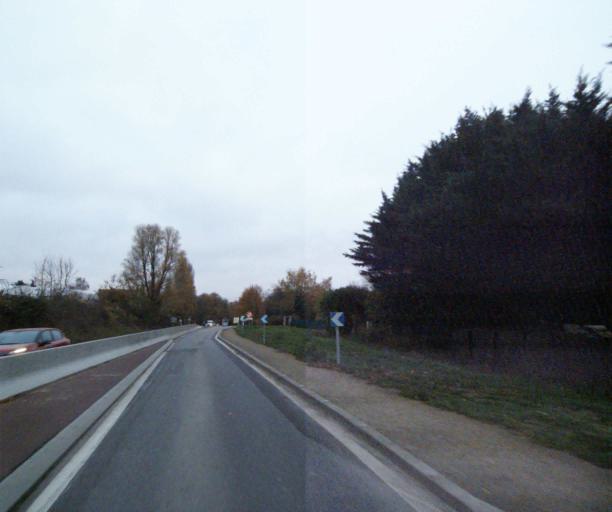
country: FR
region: Ile-de-France
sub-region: Departement des Yvelines
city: Villennes-sur-Seine
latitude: 48.9495
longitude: 1.9792
